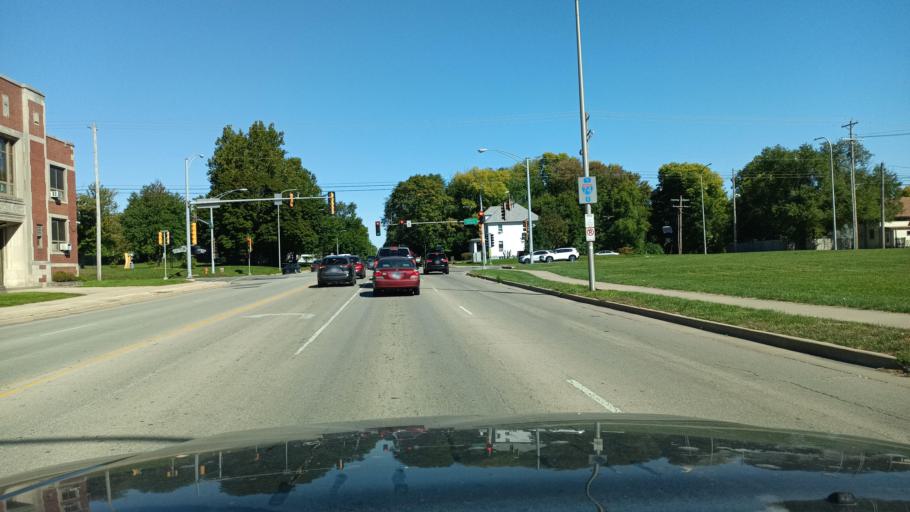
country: US
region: Illinois
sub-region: Champaign County
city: Champaign
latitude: 40.1265
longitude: -88.2435
